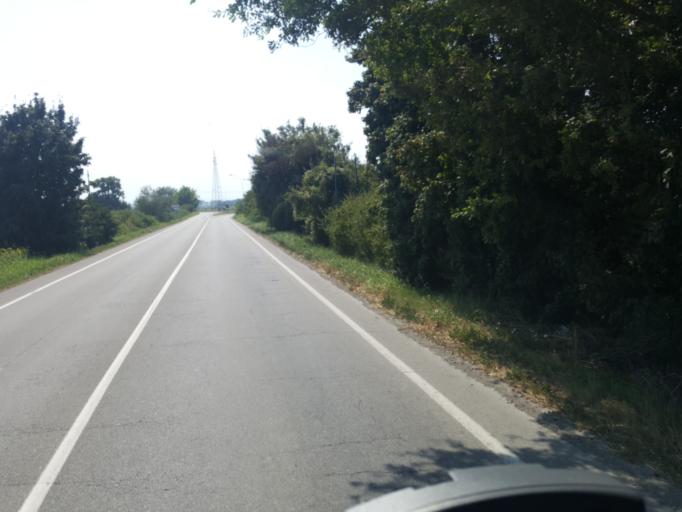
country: IT
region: Emilia-Romagna
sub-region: Provincia di Piacenza
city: Caorso
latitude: 45.0694
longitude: 9.8919
